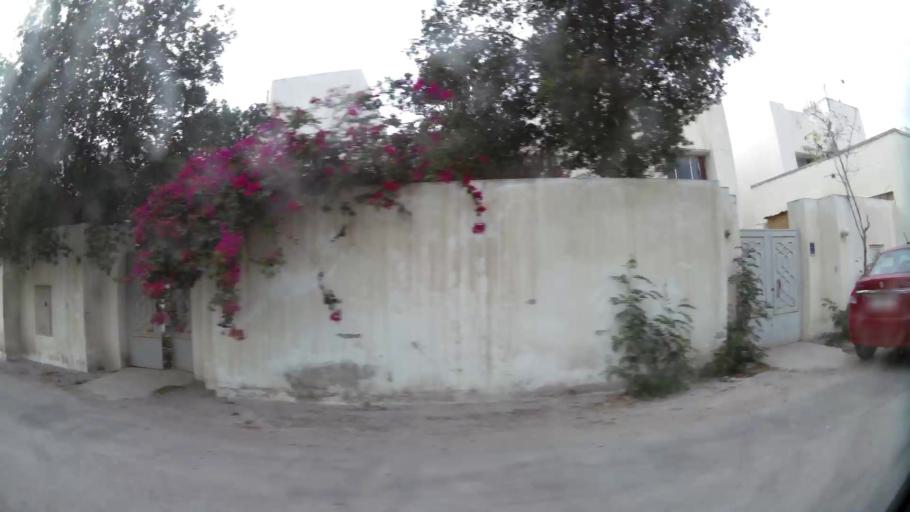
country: QA
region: Baladiyat ad Dawhah
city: Doha
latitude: 25.2701
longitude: 51.4940
